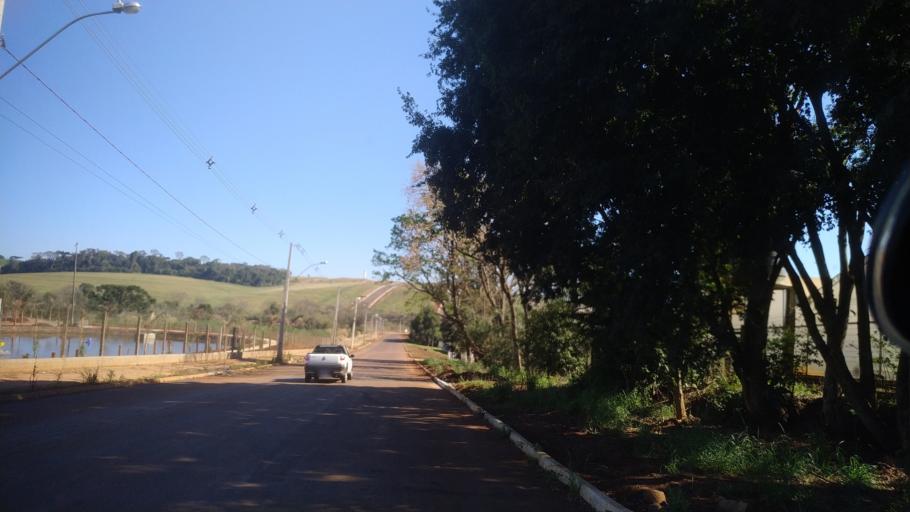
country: BR
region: Santa Catarina
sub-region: Chapeco
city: Chapeco
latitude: -27.0824
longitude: -52.6964
